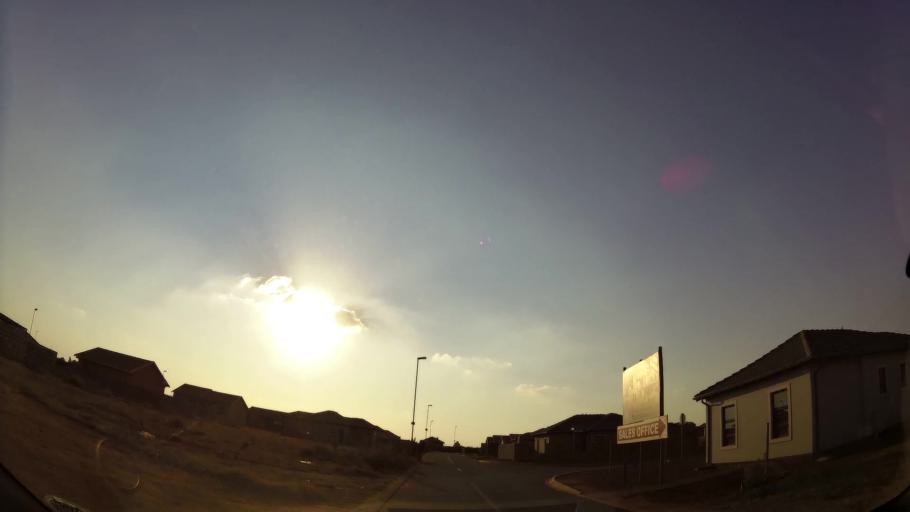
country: ZA
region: Gauteng
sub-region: Ekurhuleni Metropolitan Municipality
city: Benoni
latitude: -26.1279
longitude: 28.3791
